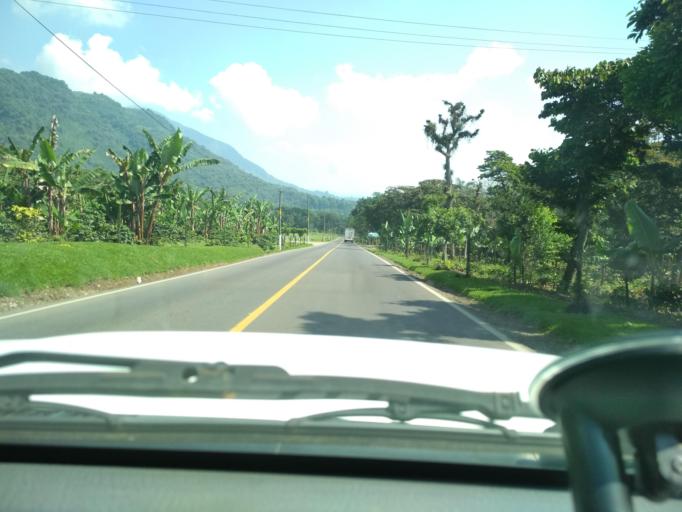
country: MX
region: Veracruz
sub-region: Fortin
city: Santa Lucia Potrerillo
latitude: 18.9787
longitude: -97.0170
